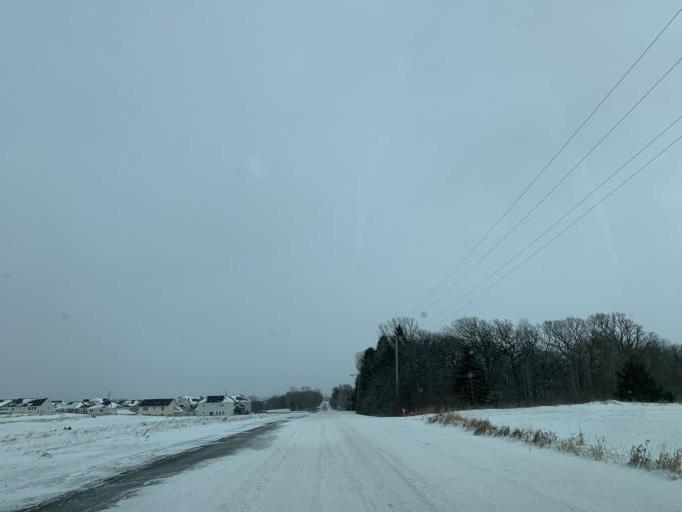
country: US
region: Minnesota
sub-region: Washington County
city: Cottage Grove
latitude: 44.8764
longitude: -92.9395
